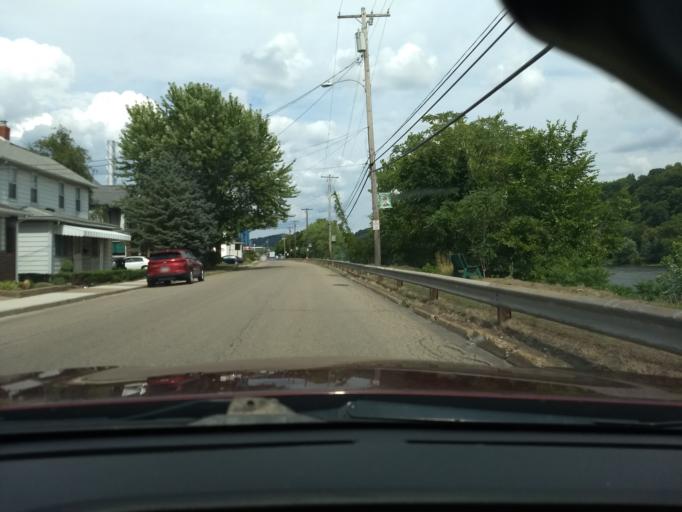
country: US
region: Pennsylvania
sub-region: Allegheny County
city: Brackenridge
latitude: 40.6035
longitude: -79.7366
